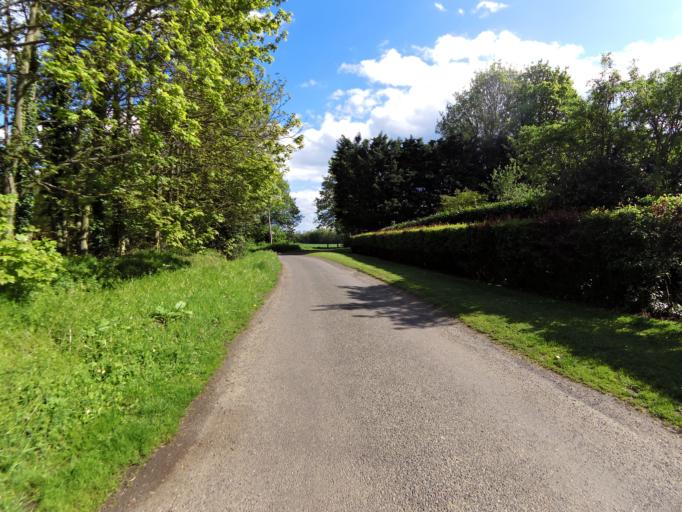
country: GB
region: England
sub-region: Suffolk
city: Thurston
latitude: 52.2419
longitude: 0.8278
